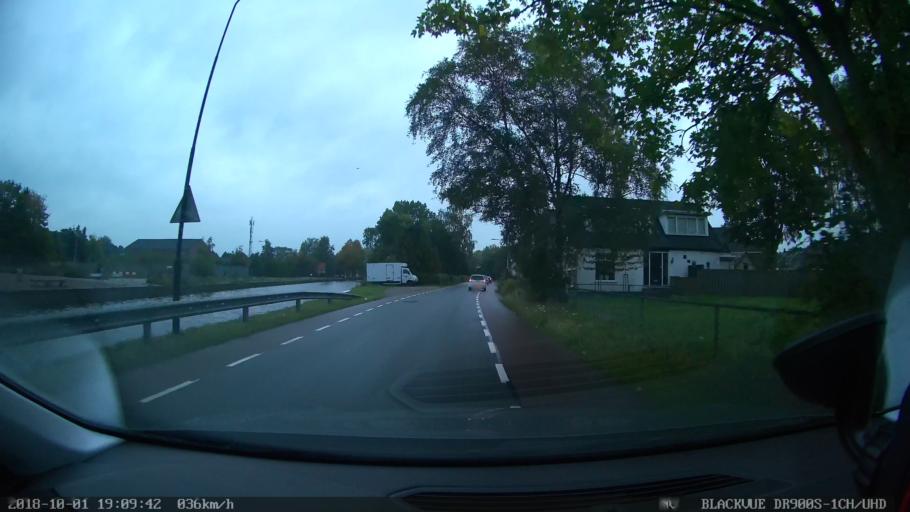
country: NL
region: Gelderland
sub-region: Gemeente Apeldoorn
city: Apeldoorn
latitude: 52.2153
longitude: 5.9784
